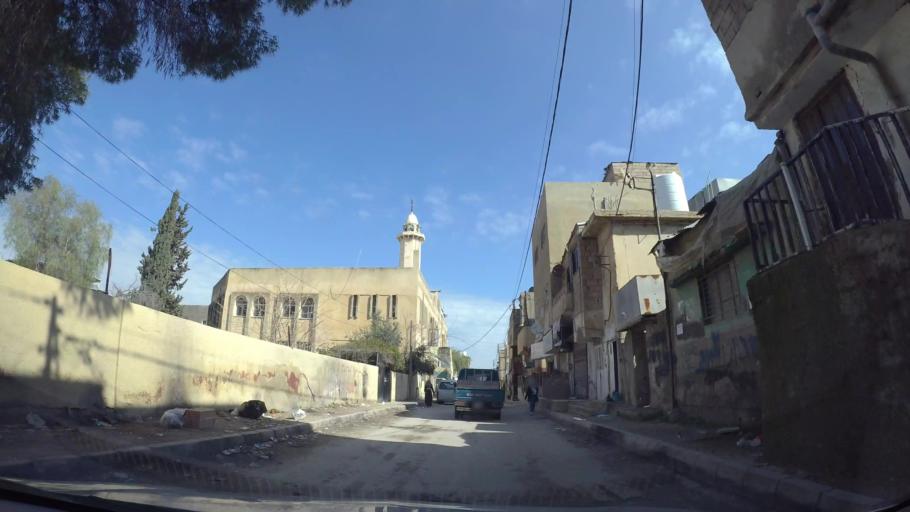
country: JO
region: Amman
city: Al Jubayhah
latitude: 32.0719
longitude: 35.8460
